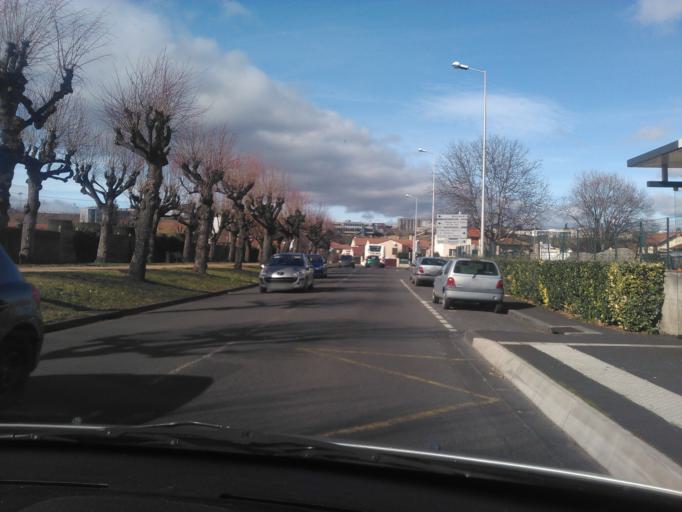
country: FR
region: Auvergne
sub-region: Departement du Puy-de-Dome
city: Aubiere
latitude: 45.7541
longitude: 3.1165
